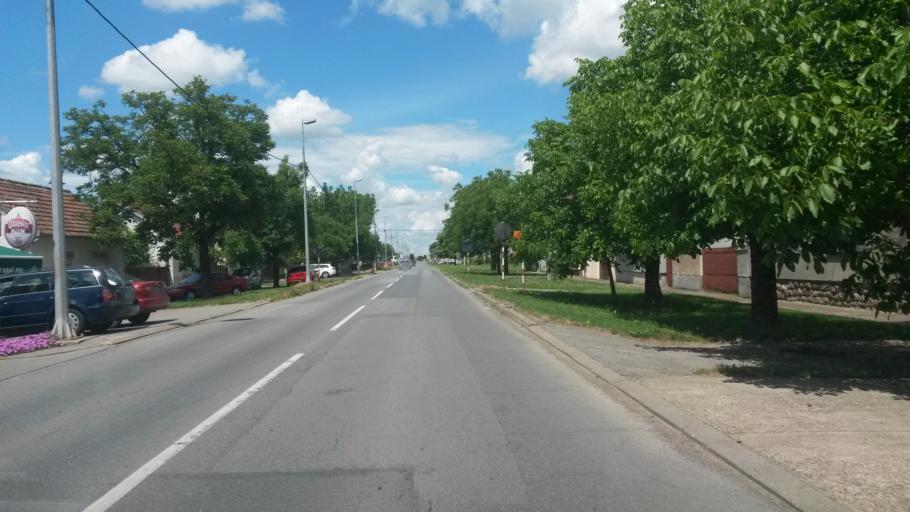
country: HR
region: Osjecko-Baranjska
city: Viskovci
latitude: 45.3302
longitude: 18.4192
